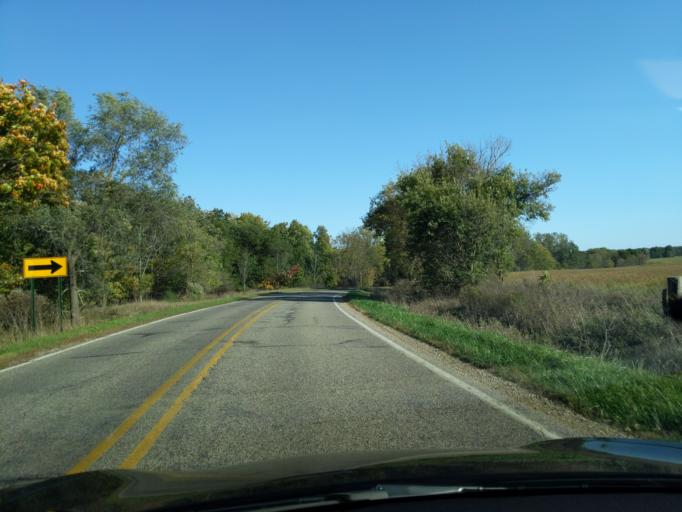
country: US
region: Michigan
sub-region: Clinton County
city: Saint Johns
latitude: 42.9289
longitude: -84.4785
